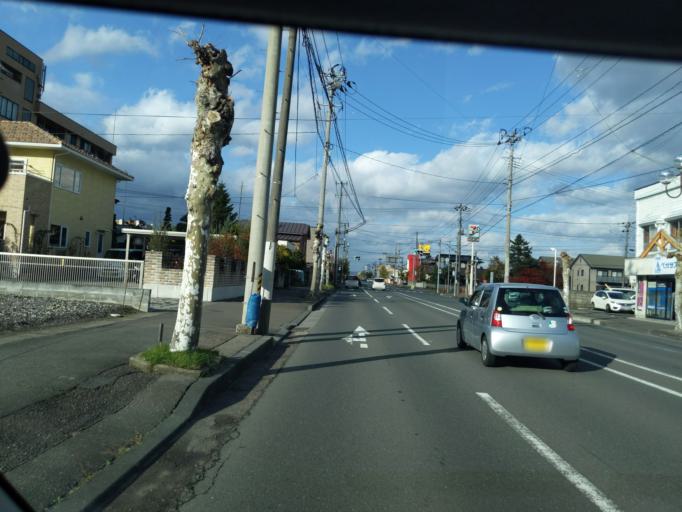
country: JP
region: Iwate
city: Mizusawa
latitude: 39.1348
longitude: 141.1552
